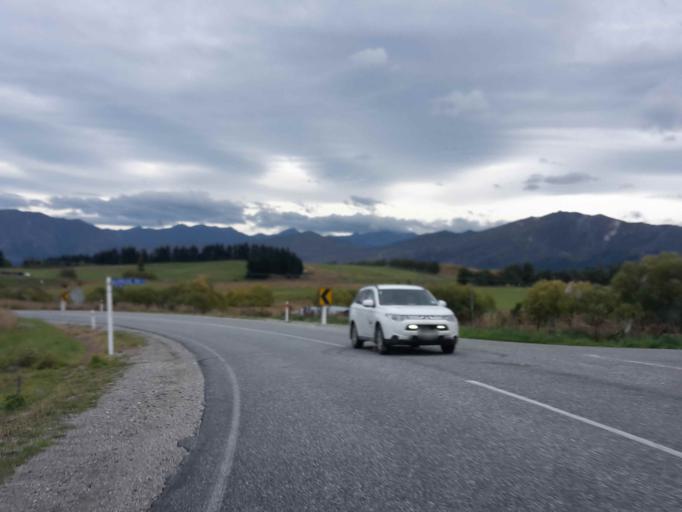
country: NZ
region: Otago
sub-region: Queenstown-Lakes District
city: Arrowtown
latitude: -44.9737
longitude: 168.8851
